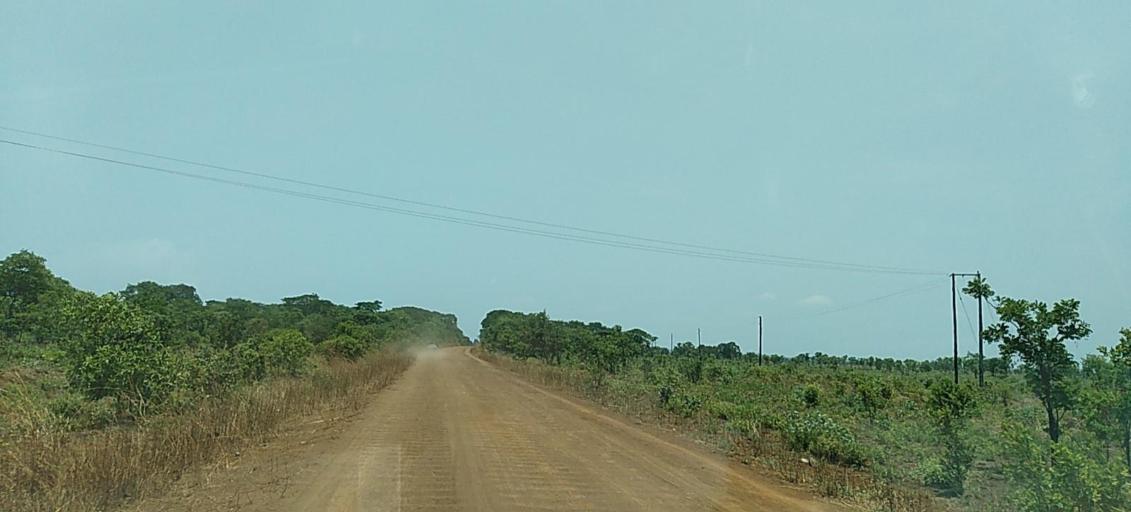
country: ZM
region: Copperbelt
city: Mpongwe
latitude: -13.6916
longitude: 27.8623
